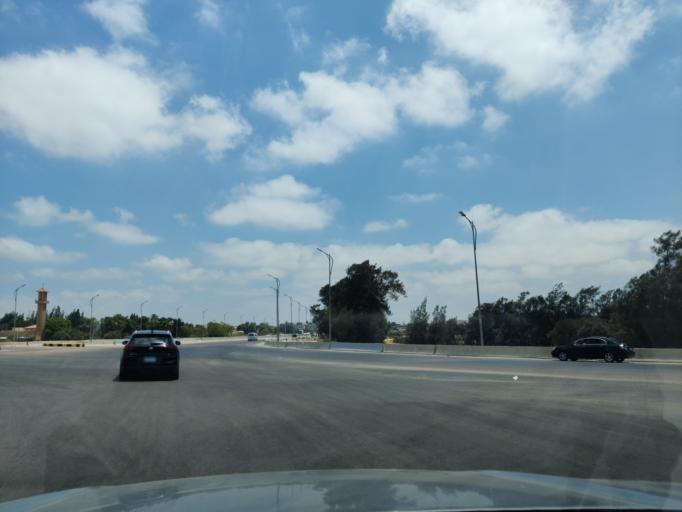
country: EG
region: Alexandria
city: Alexandria
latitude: 30.9751
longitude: 29.6616
